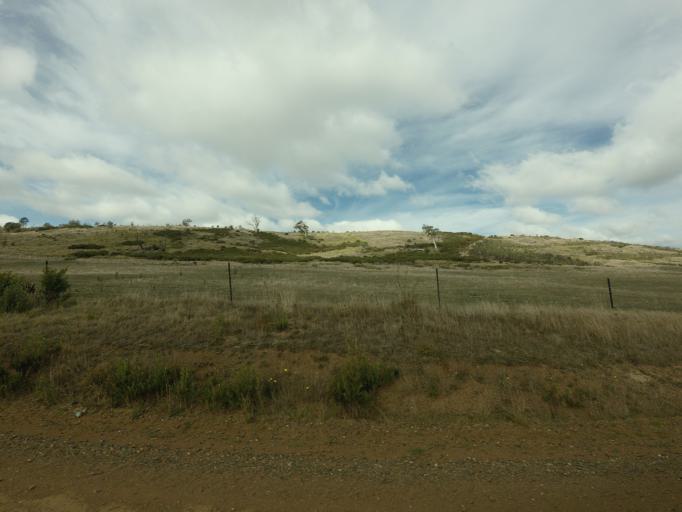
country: AU
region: Tasmania
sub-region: Brighton
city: Bridgewater
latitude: -42.4156
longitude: 147.3957
